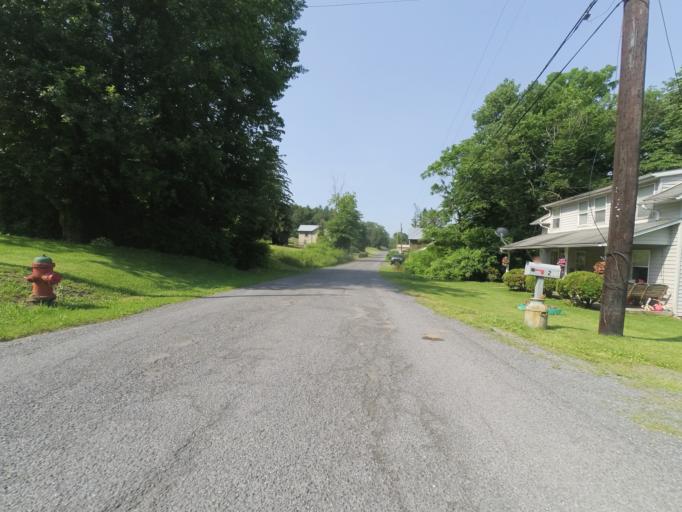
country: US
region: Pennsylvania
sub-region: Centre County
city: Zion
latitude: 40.9820
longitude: -77.7057
